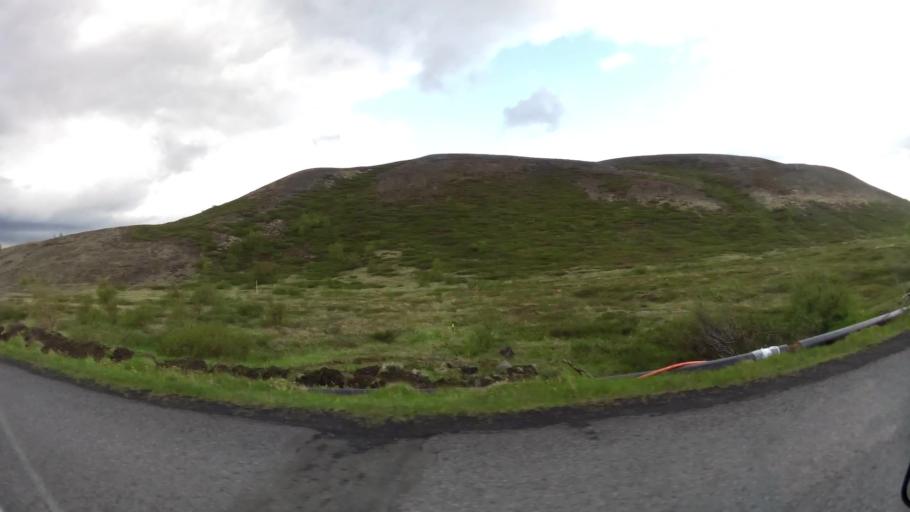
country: IS
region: Northeast
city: Laugar
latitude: 65.6425
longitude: -16.9054
